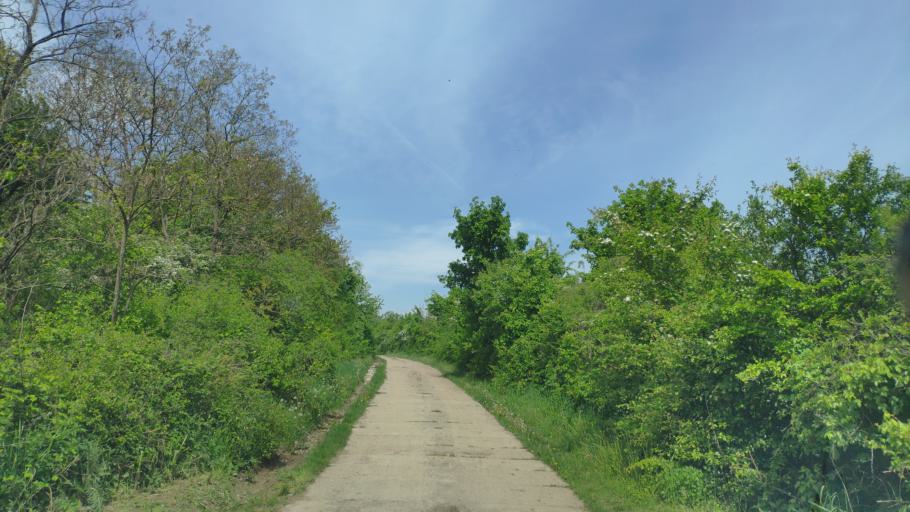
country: SK
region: Kosicky
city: Secovce
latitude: 48.6868
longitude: 21.6066
